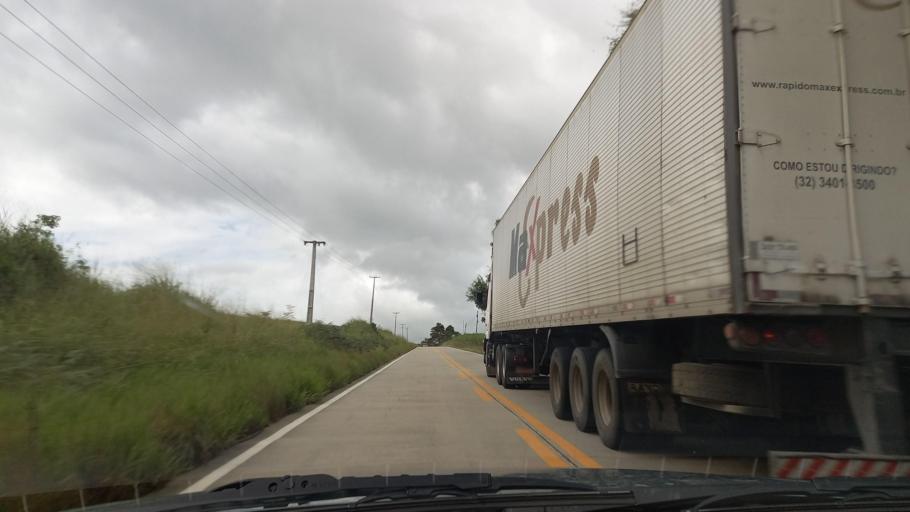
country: BR
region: Pernambuco
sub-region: Quipapa
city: Quipapa
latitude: -8.8000
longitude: -35.9998
